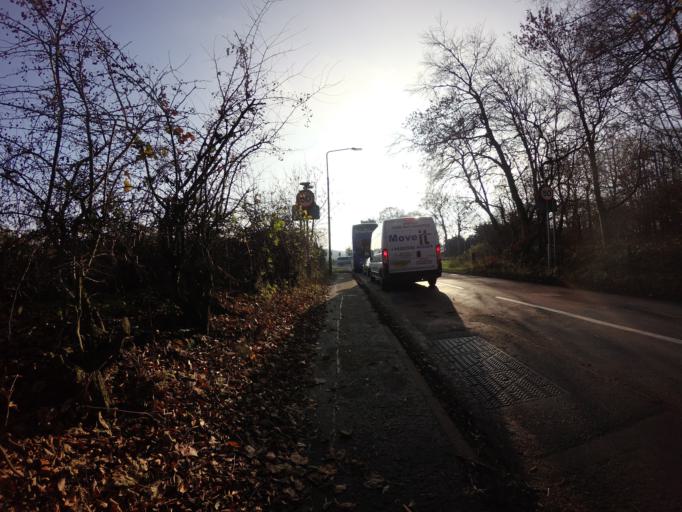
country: GB
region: Scotland
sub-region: West Lothian
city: Livingston
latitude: 55.9243
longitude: -3.5106
